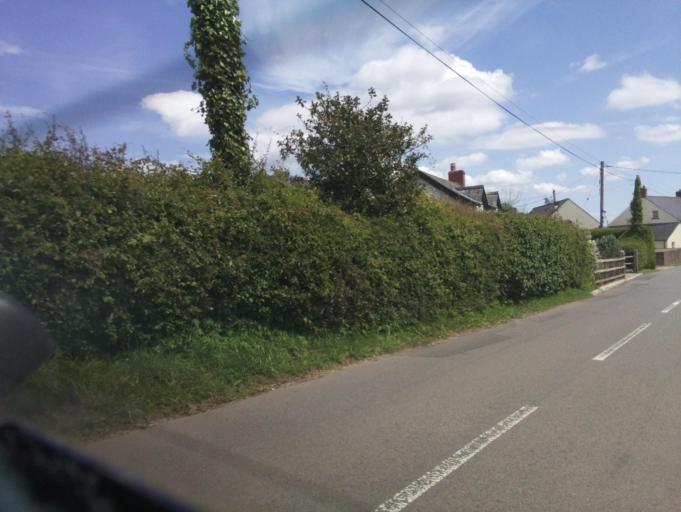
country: GB
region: England
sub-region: Herefordshire
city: Llanrothal
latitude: 51.8503
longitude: -2.7993
